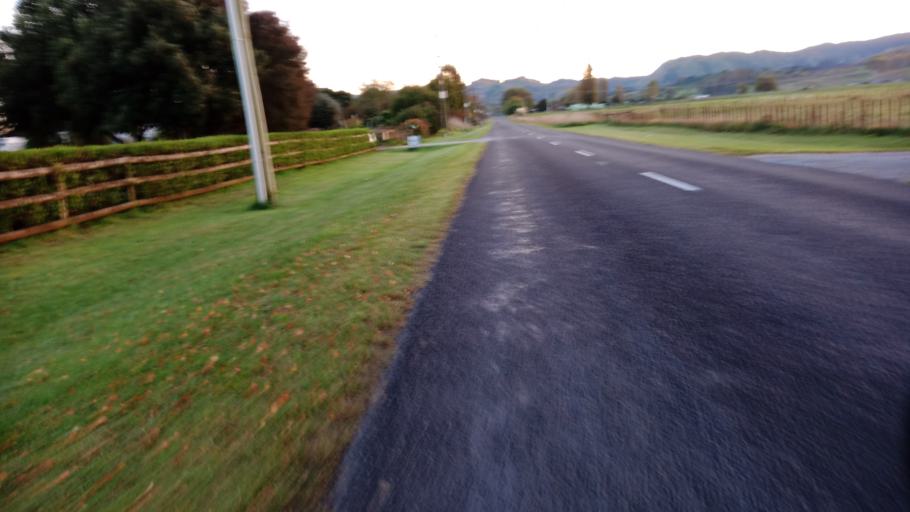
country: NZ
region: Gisborne
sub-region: Gisborne District
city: Gisborne
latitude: -38.6414
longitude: 177.9827
